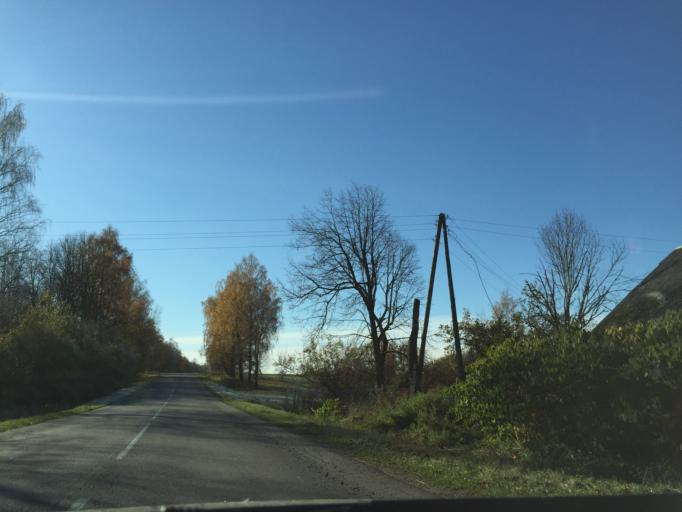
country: LV
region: Skriveri
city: Skriveri
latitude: 56.6855
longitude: 25.1449
